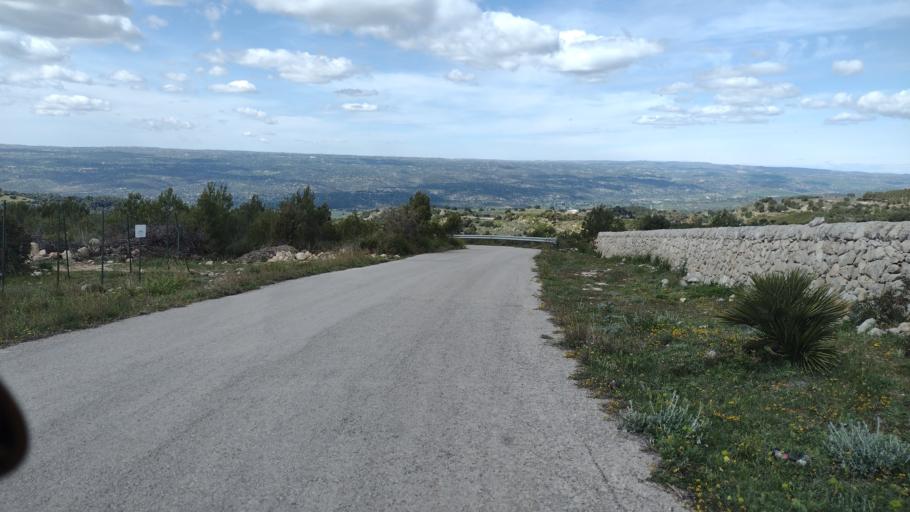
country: IT
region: Sicily
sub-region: Provincia di Siracusa
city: Noto
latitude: 36.9170
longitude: 14.9810
